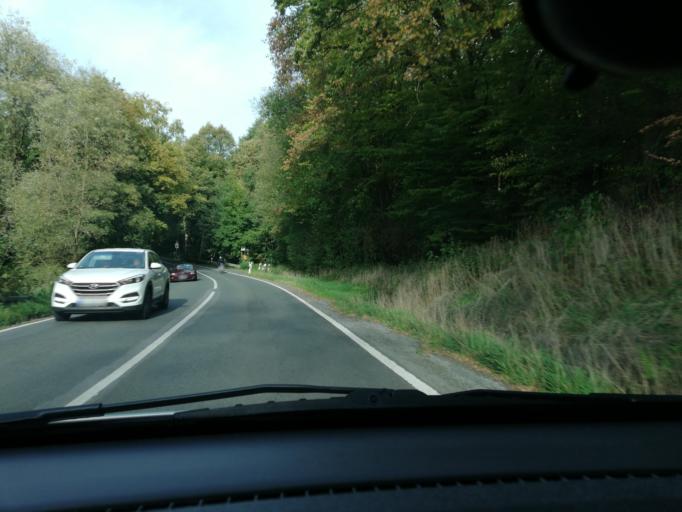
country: DE
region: North Rhine-Westphalia
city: Sprockhovel
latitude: 51.3525
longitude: 7.2550
